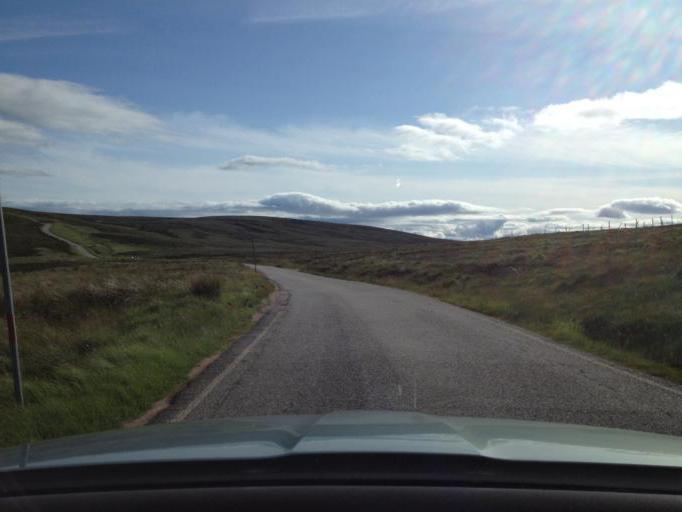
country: GB
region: Scotland
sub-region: Aberdeenshire
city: Laurencekirk
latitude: 56.9288
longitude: -2.5772
